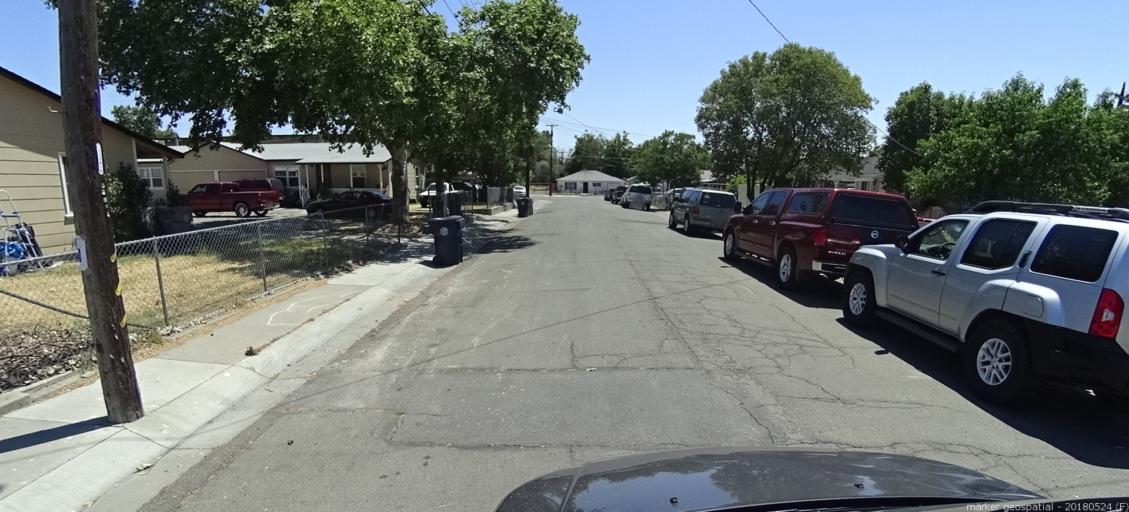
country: US
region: California
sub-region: Sacramento County
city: Sacramento
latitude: 38.6157
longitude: -121.4546
